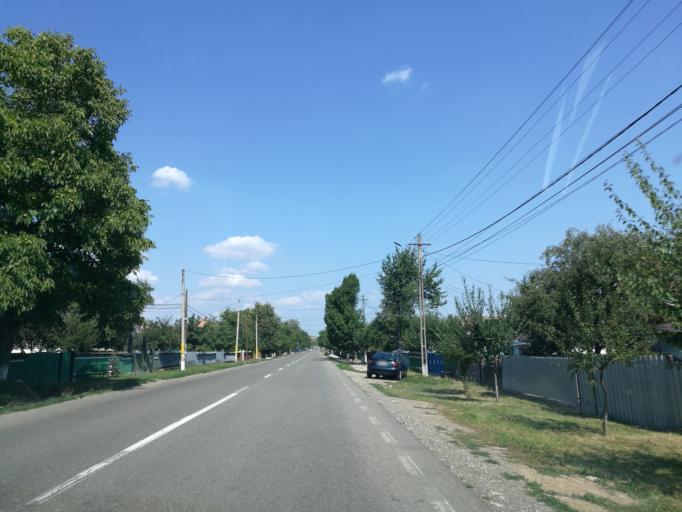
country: RO
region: Neamt
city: Bodesti
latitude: 47.0396
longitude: 26.4081
